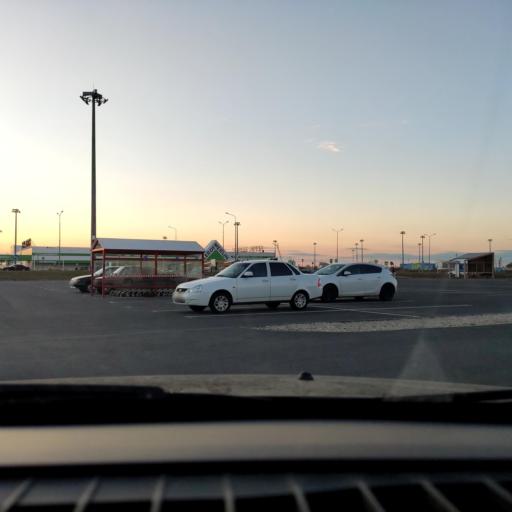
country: RU
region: Samara
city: Tol'yatti
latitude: 53.5493
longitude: 49.3435
